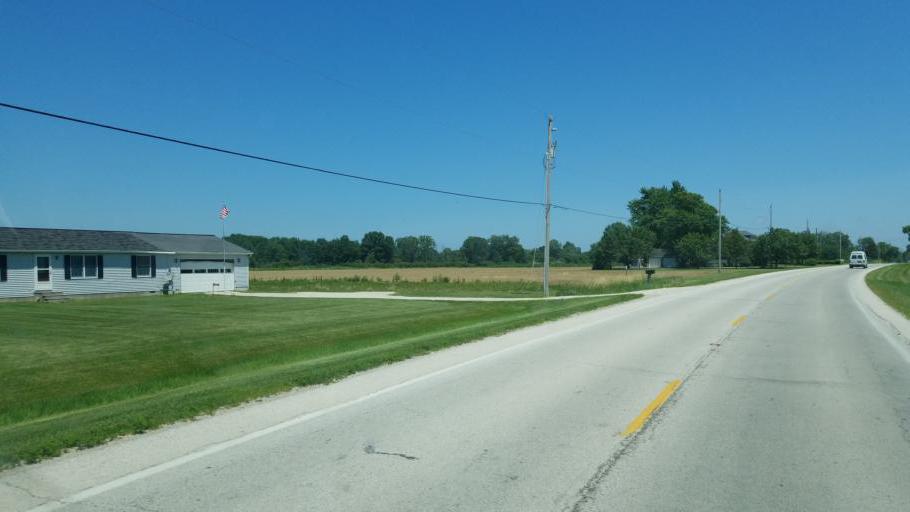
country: US
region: Ohio
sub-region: Ottawa County
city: Port Clinton
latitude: 41.5175
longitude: -83.0301
